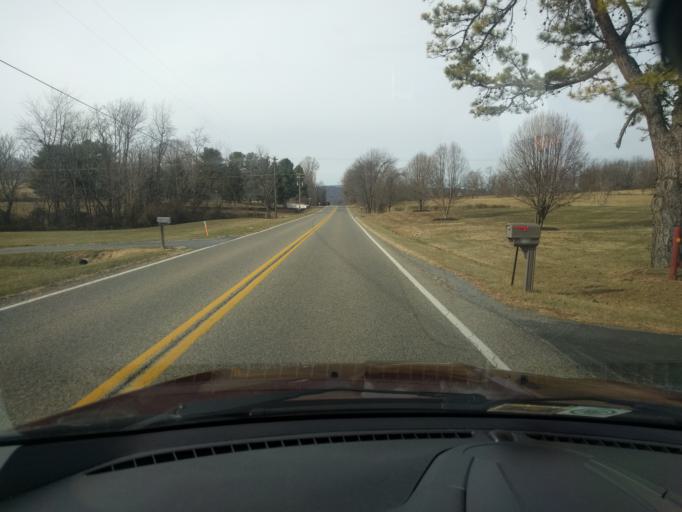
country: US
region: Virginia
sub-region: Augusta County
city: Stuarts Draft
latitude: 38.0361
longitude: -79.0723
